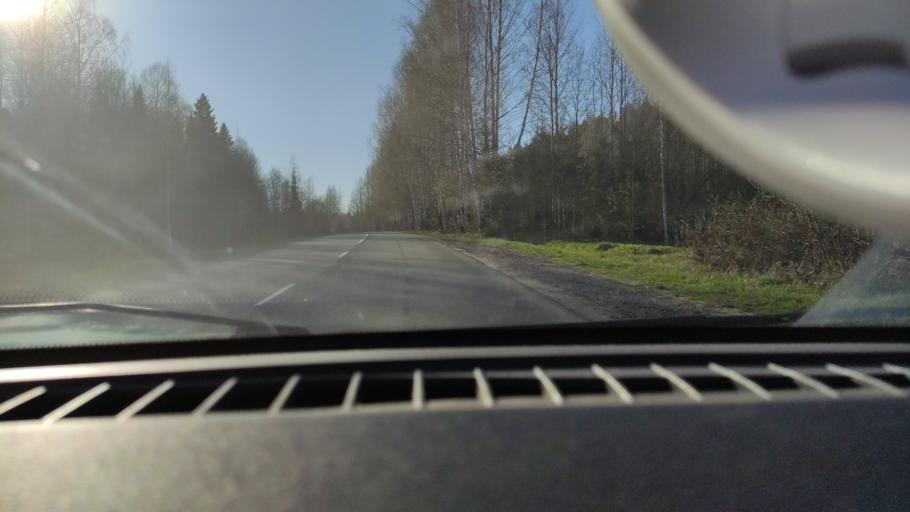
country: RU
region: Perm
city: Polazna
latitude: 58.1228
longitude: 56.4436
